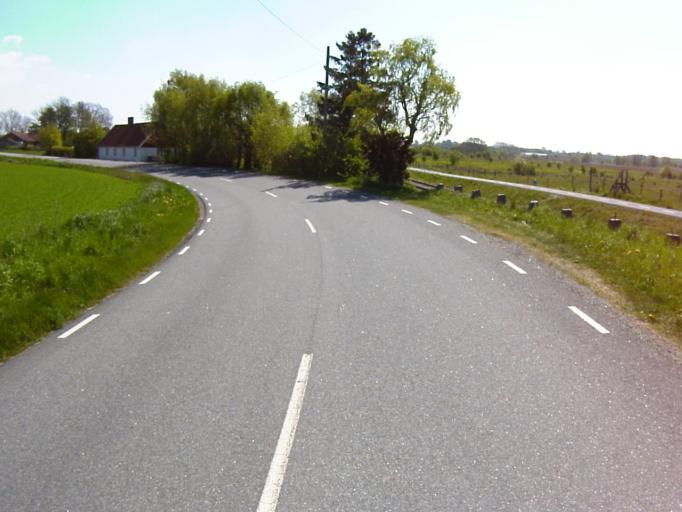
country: SE
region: Skane
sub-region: Kristianstads Kommun
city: Fjalkinge
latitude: 56.0080
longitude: 14.2500
